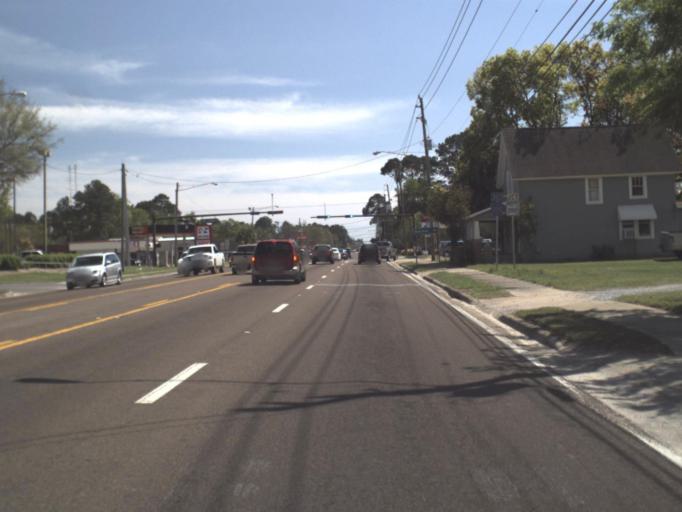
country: US
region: Florida
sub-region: Bay County
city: Lynn Haven
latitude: 30.2387
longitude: -85.6488
